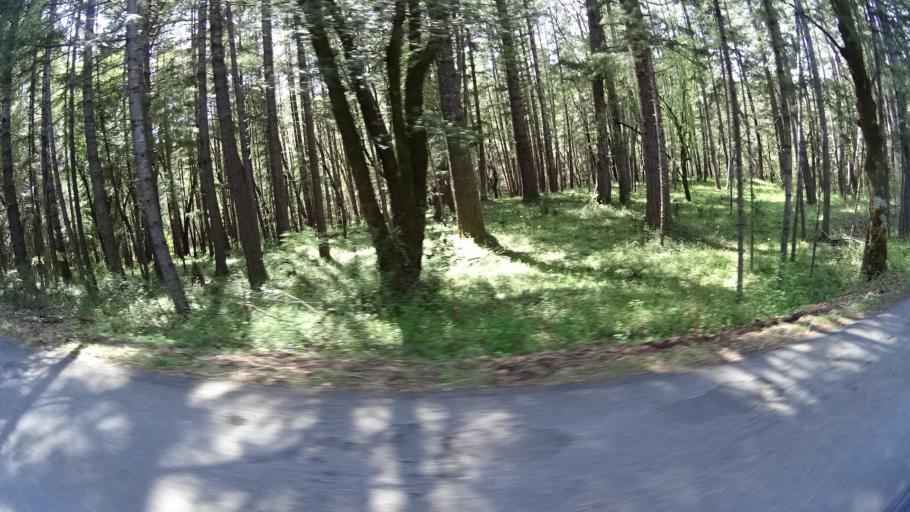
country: US
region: California
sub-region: Humboldt County
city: Redway
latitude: 40.2804
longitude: -123.6430
